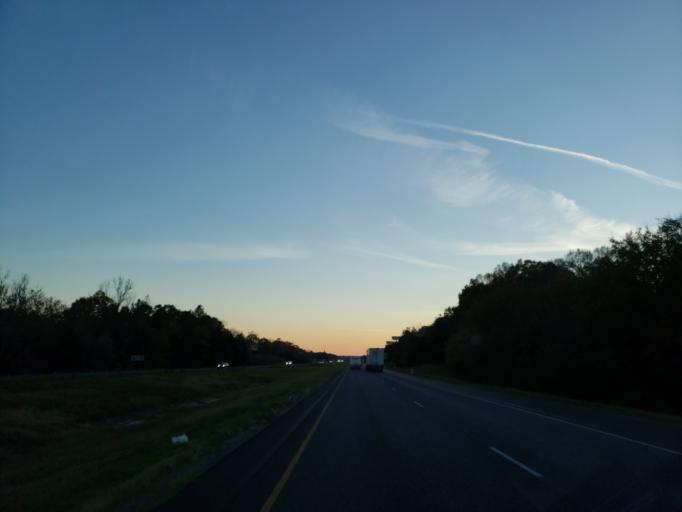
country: US
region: Alabama
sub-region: Sumter County
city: Livingston
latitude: 32.6393
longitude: -88.2005
